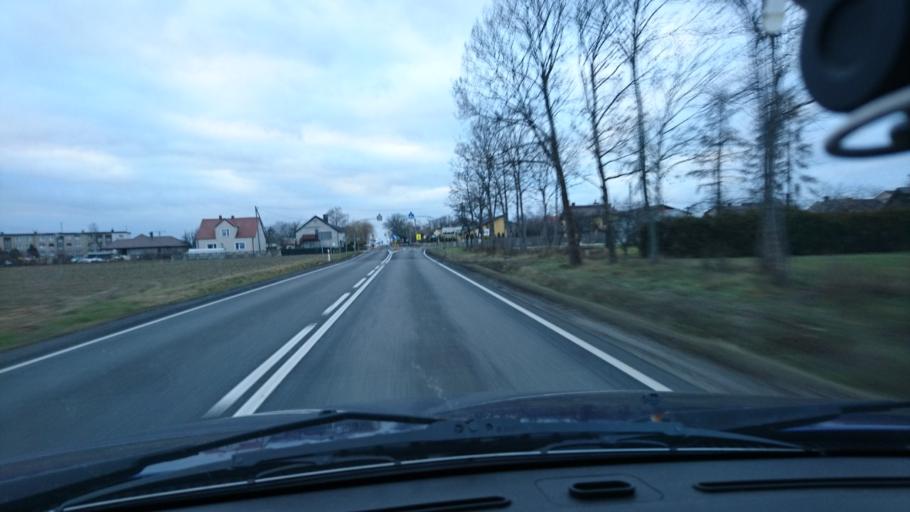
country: PL
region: Greater Poland Voivodeship
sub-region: Powiat kepinski
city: Slupia pod Kepnem
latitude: 51.2380
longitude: 18.0446
